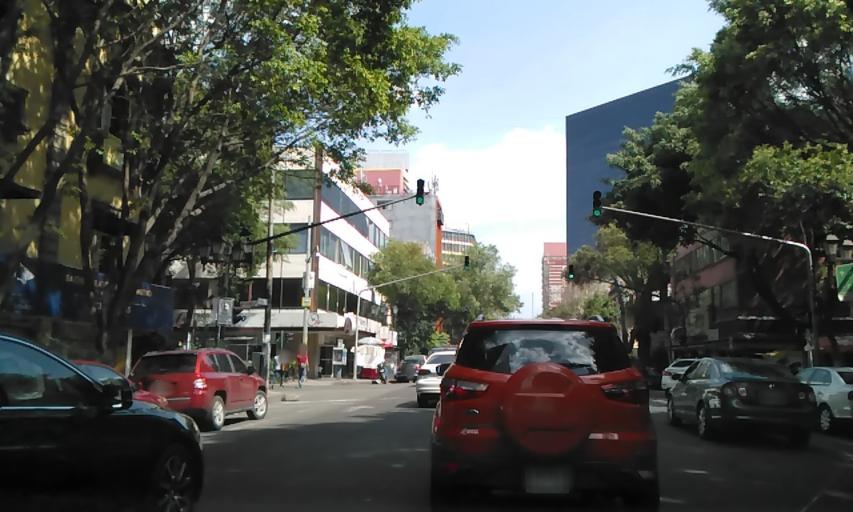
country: MX
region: Mexico City
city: Cuauhtemoc
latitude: 19.4274
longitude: -99.1630
